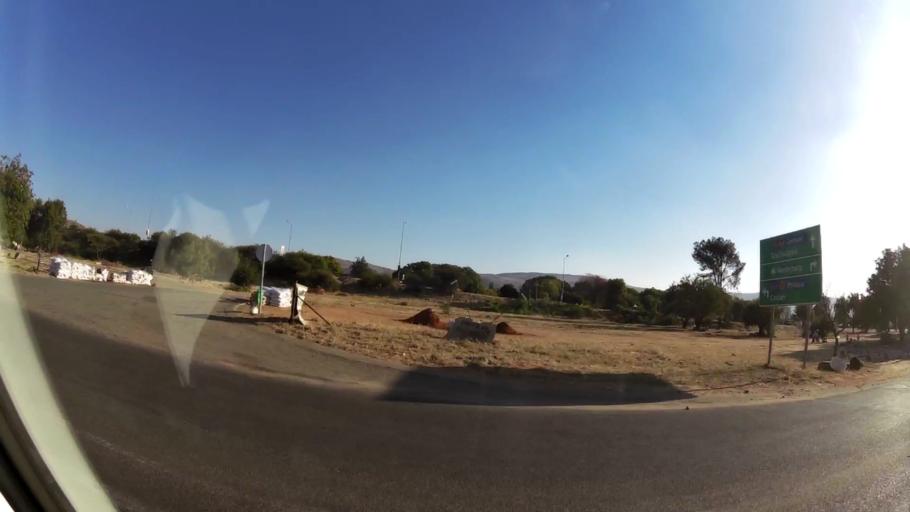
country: ZA
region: North-West
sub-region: Bojanala Platinum District Municipality
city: Rustenburg
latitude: -25.6871
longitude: 27.2264
